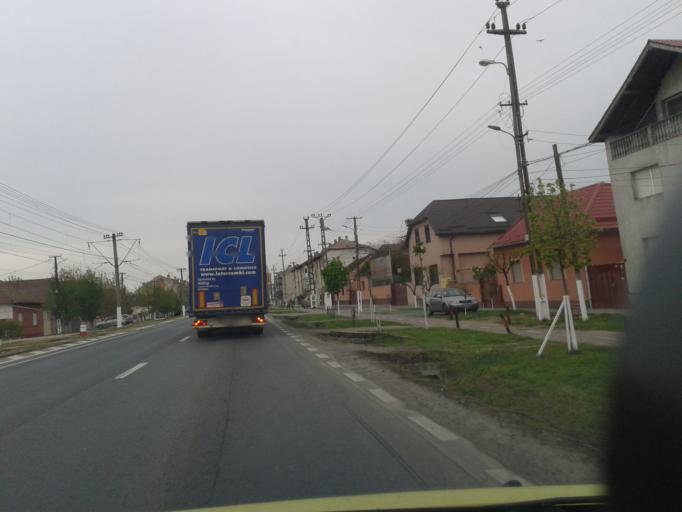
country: RO
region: Arad
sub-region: Comuna Vladimirescu
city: Vladimirescu
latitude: 46.1649
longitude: 21.4001
